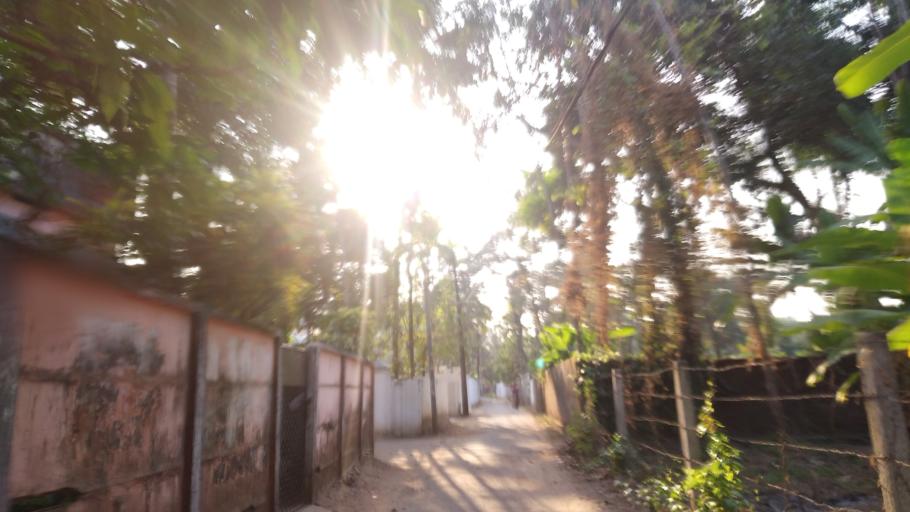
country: IN
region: Kerala
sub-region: Ernakulam
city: Elur
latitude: 10.0881
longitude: 76.2113
